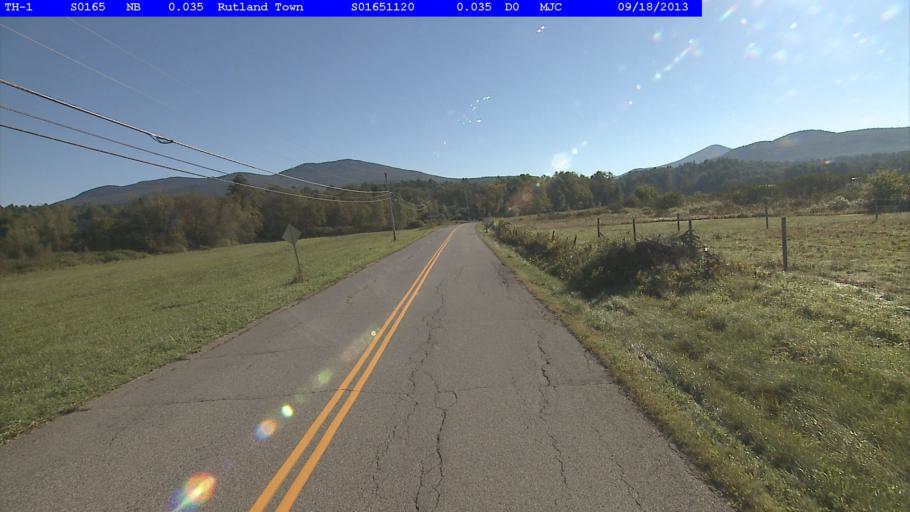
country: US
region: Vermont
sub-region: Rutland County
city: Rutland
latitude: 43.6517
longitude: -72.9715
